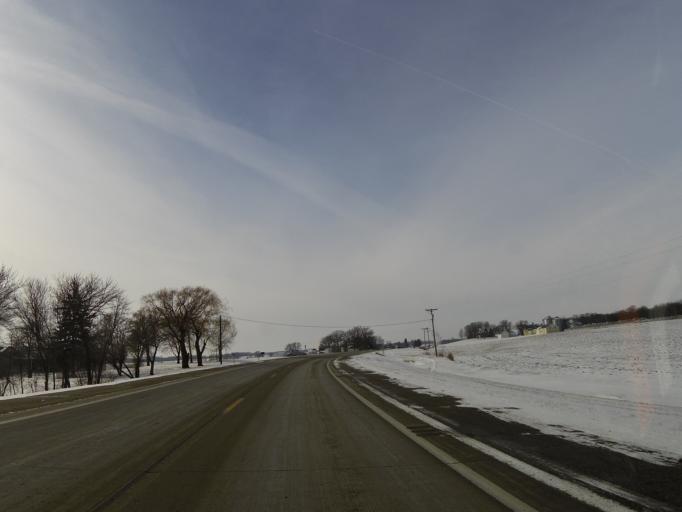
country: US
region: Minnesota
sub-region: McLeod County
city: Hutchinson
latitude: 44.8928
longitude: -94.2289
